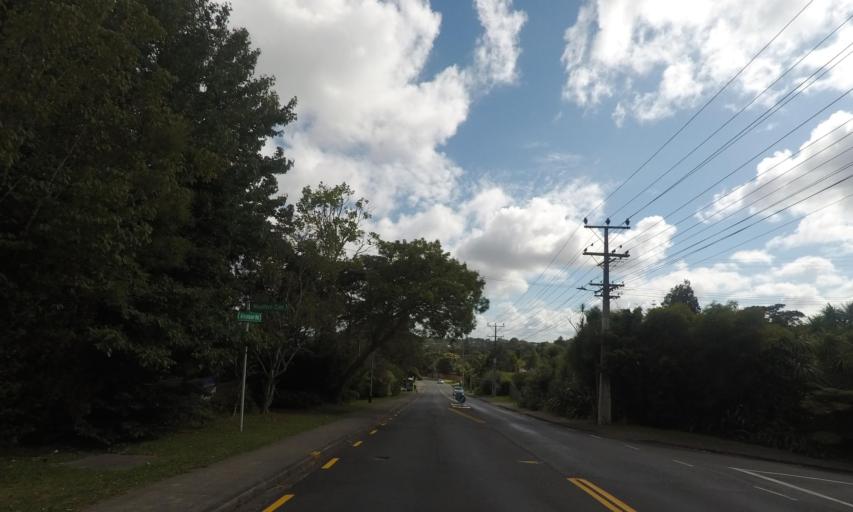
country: NZ
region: Auckland
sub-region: Auckland
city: Titirangi
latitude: -36.9335
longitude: 174.6551
